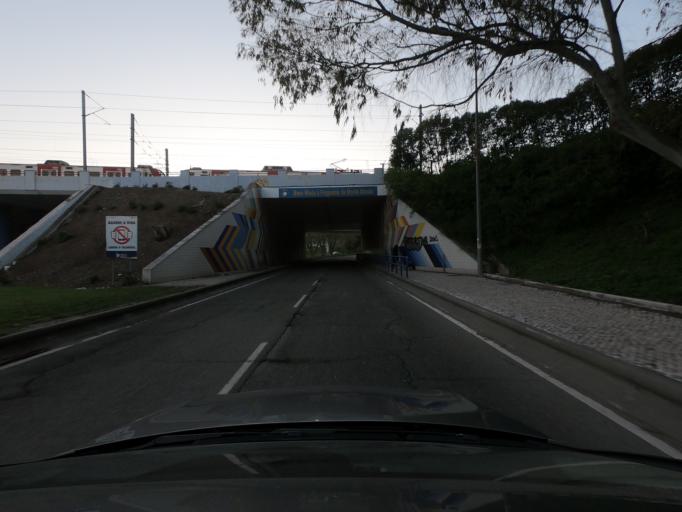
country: PT
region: Lisbon
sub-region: Sintra
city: Queluz
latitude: 38.7540
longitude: -9.2656
